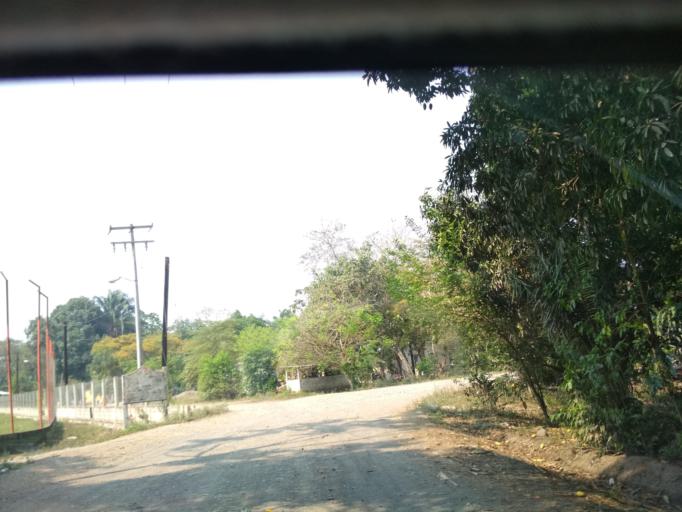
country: MX
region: Oaxaca
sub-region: Acatlan de Perez Figueroa
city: Zona Urbana Ejidal
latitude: 18.5894
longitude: -96.5552
